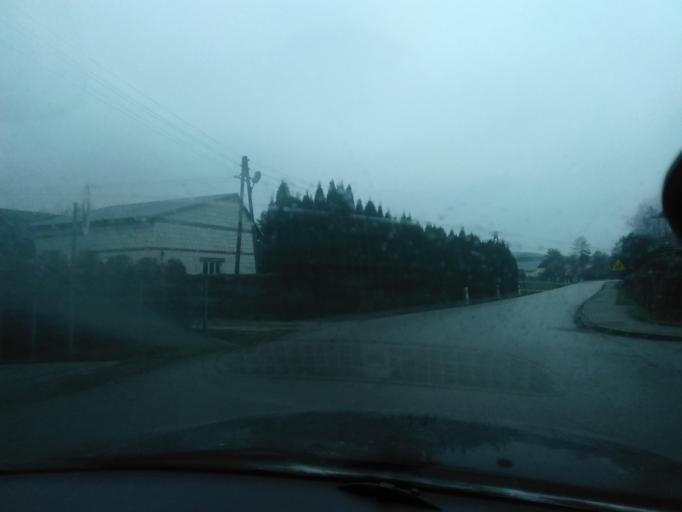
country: PL
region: Subcarpathian Voivodeship
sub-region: Powiat jaroslawski
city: Pawlosiow
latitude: 49.9530
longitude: 22.5959
